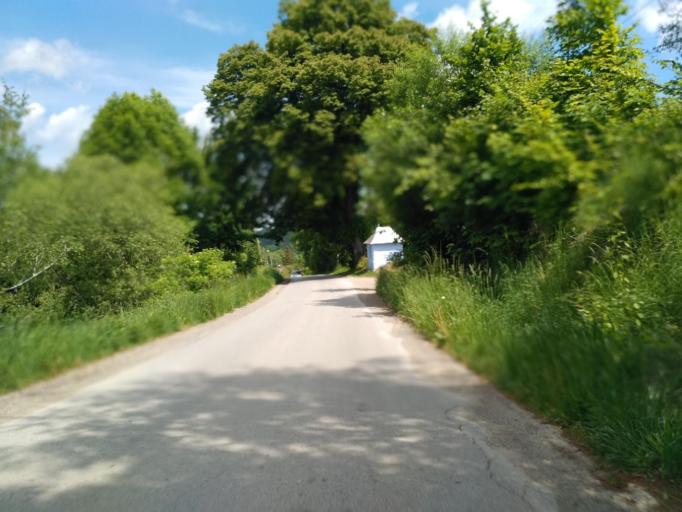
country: PL
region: Subcarpathian Voivodeship
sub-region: Powiat krosnienski
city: Dukla
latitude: 49.5752
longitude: 21.6192
